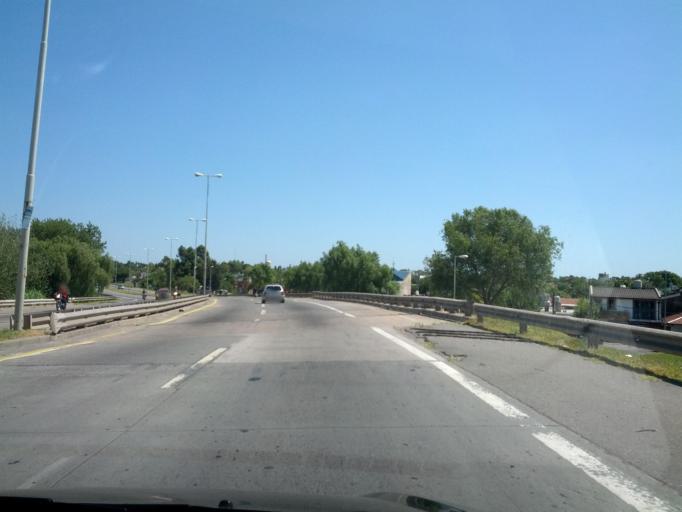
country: AR
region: Buenos Aires
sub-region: Partido de Campana
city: Campana
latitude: -34.1711
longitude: -58.9717
